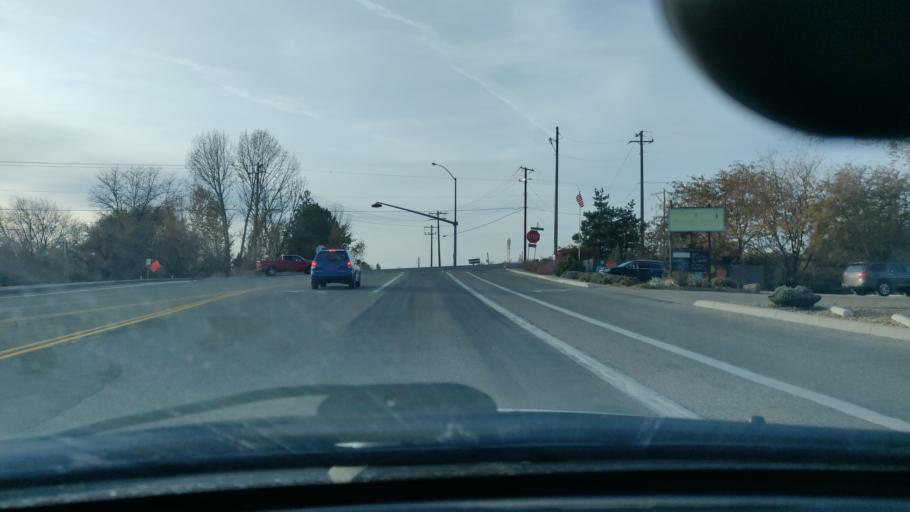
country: US
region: Idaho
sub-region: Ada County
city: Eagle
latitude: 43.6921
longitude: -116.3131
